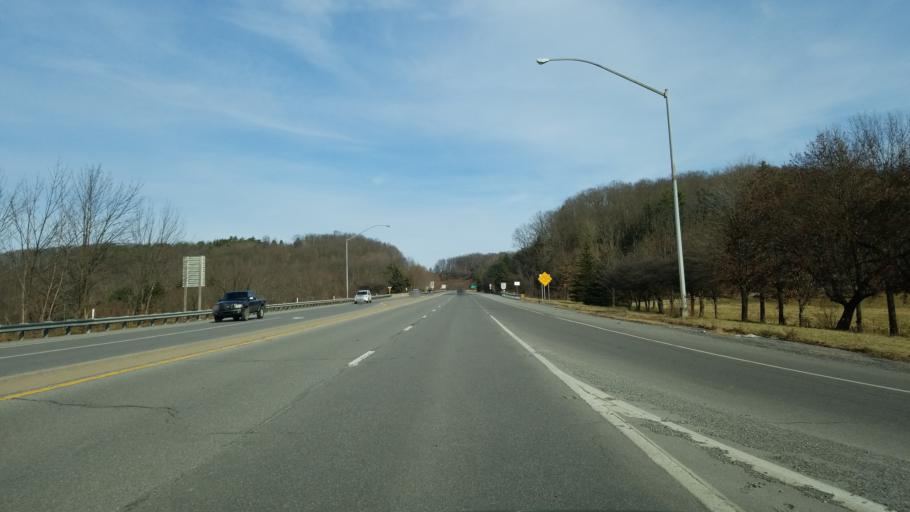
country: US
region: Pennsylvania
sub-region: Clearfield County
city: Clearfield
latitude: 41.0083
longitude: -78.4346
